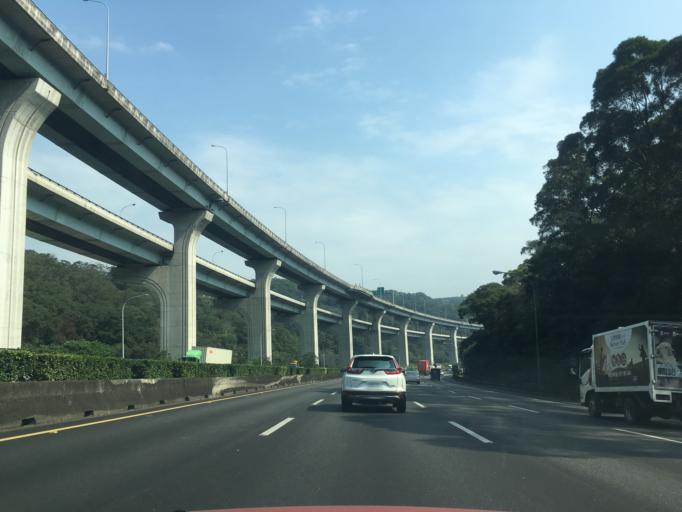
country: TW
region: Taipei
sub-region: Taipei
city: Banqiao
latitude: 25.0650
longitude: 121.3864
